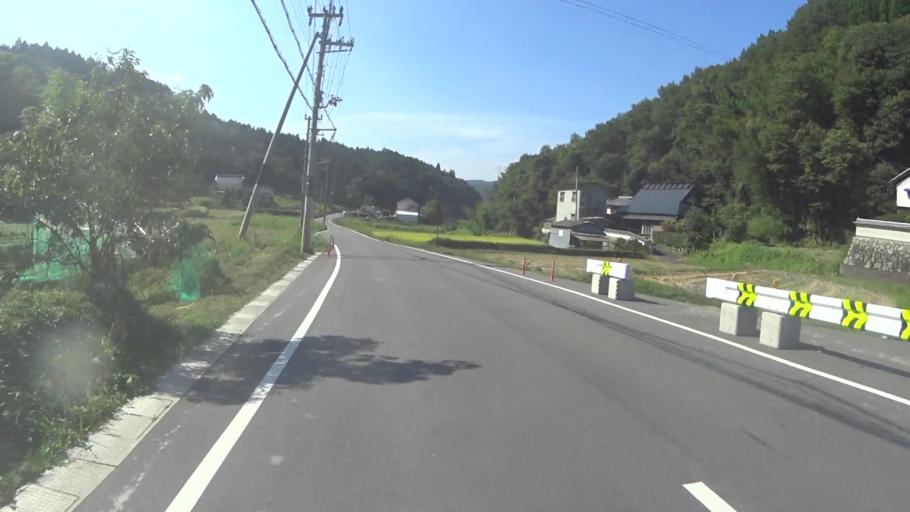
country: JP
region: Kyoto
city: Kameoka
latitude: 34.9527
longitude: 135.5390
